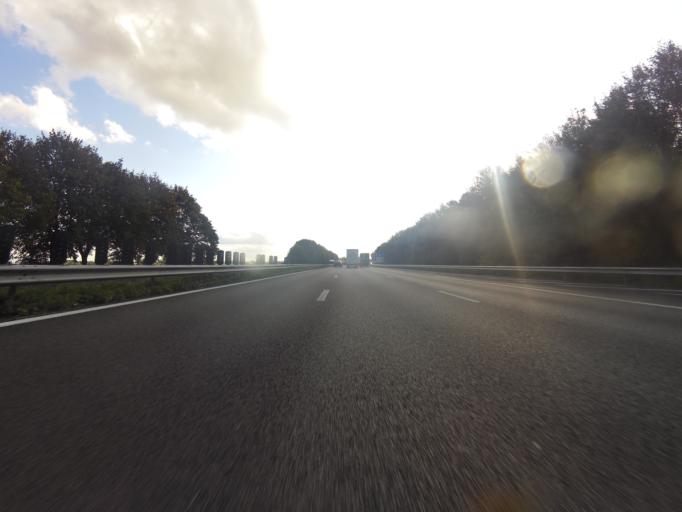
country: FR
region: Picardie
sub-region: Departement de la Somme
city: Peronne
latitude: 49.9005
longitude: 2.8475
